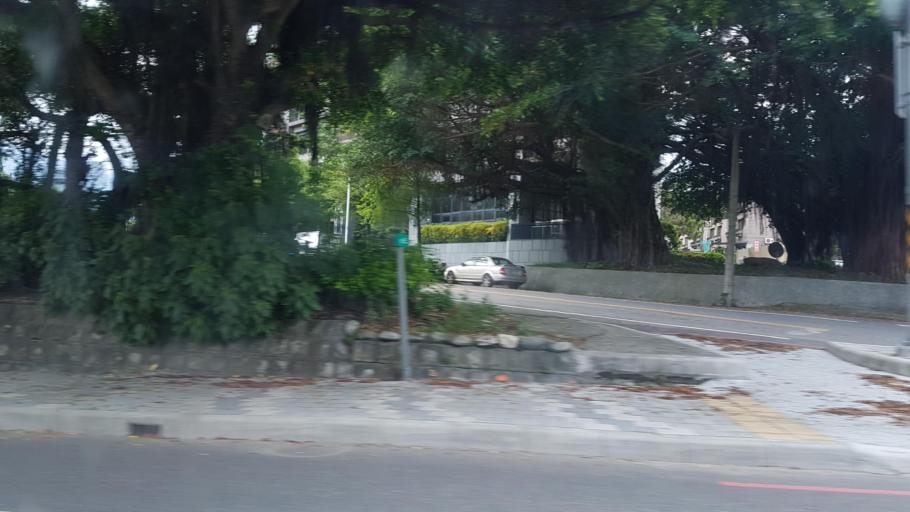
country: TW
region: Taiwan
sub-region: Hualien
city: Hualian
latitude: 23.9812
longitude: 121.6198
